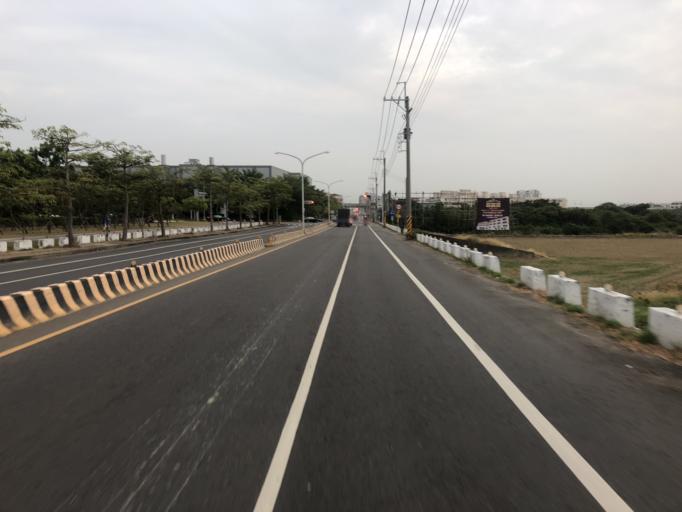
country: TW
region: Taiwan
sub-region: Tainan
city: Tainan
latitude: 23.0835
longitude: 120.2819
